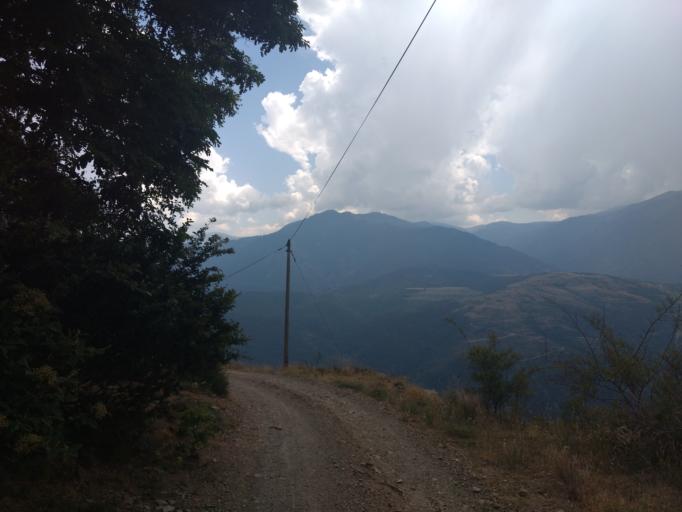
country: FR
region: Languedoc-Roussillon
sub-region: Departement des Pyrenees-Orientales
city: Vernet-les-Bains
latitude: 42.5764
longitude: 2.2876
